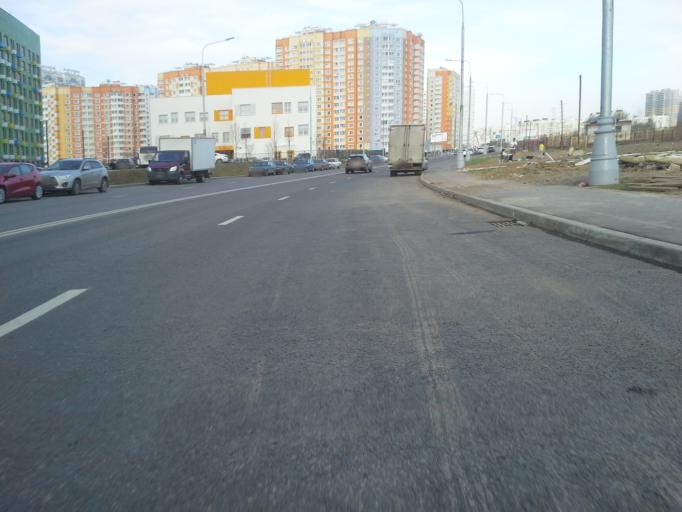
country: RU
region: Moskovskaya
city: Kommunarka
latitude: 55.5403
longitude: 37.4855
